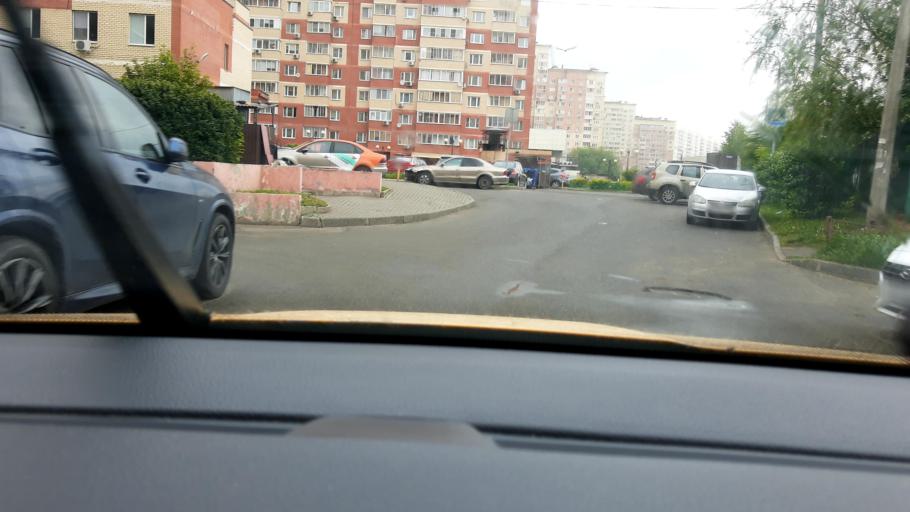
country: RU
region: Moscow
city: Vatutino
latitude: 55.9040
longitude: 37.7002
